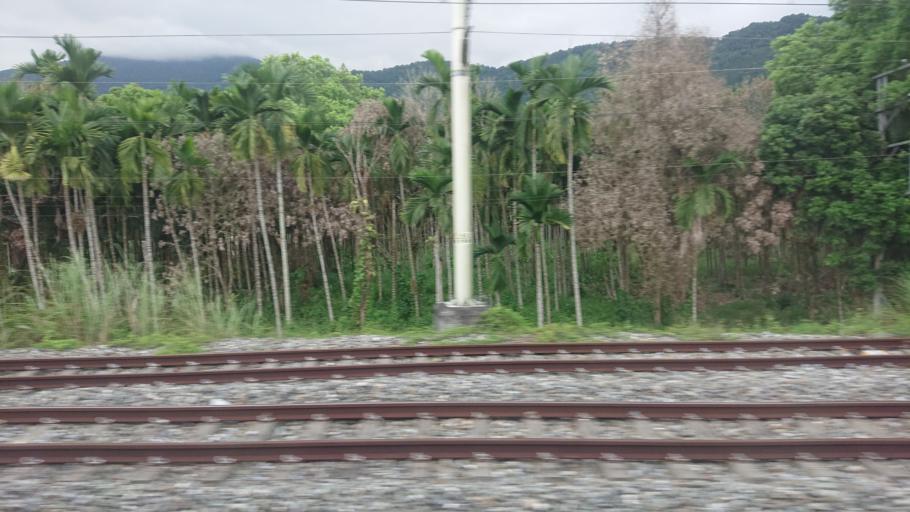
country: TW
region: Taiwan
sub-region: Hualien
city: Hualian
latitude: 23.6641
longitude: 121.4201
